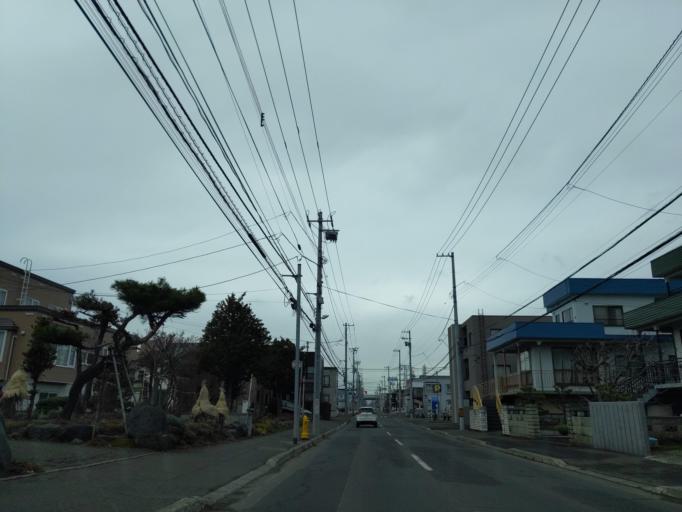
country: JP
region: Hokkaido
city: Sapporo
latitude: 43.0898
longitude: 141.3998
